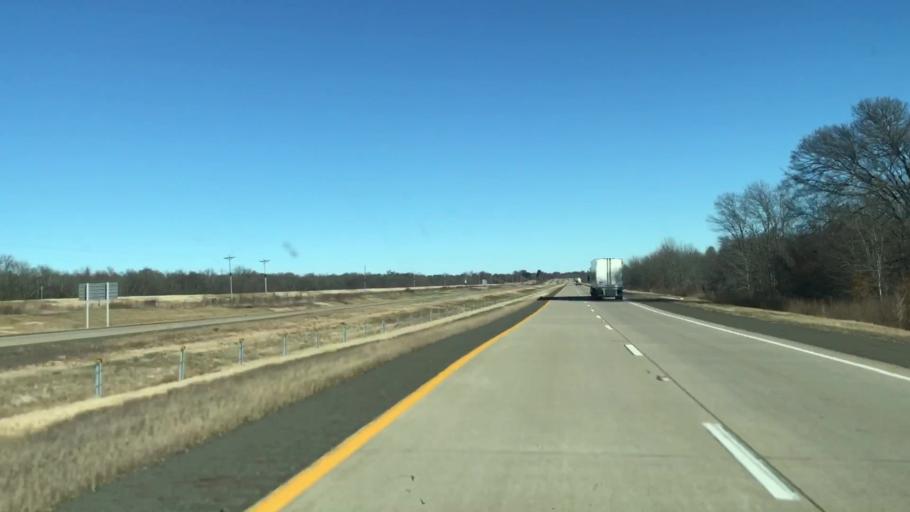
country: US
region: Texas
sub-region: Cass County
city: Queen City
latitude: 33.1364
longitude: -93.8944
